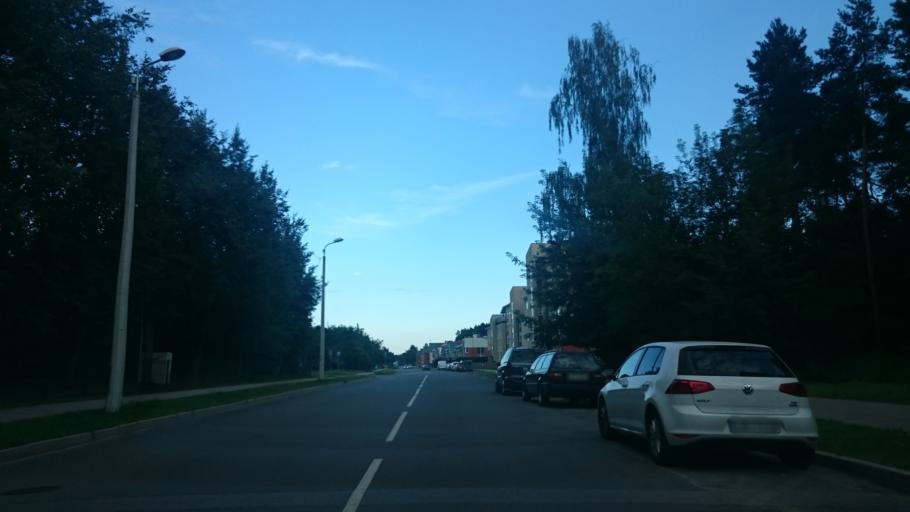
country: LV
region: Riga
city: Bergi
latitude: 56.9868
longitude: 24.2313
